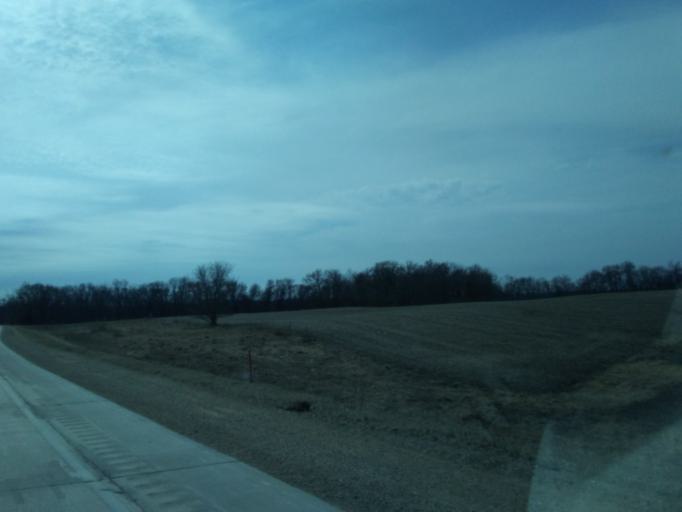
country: US
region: Iowa
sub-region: Winneshiek County
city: Decorah
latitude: 43.3449
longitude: -91.8074
